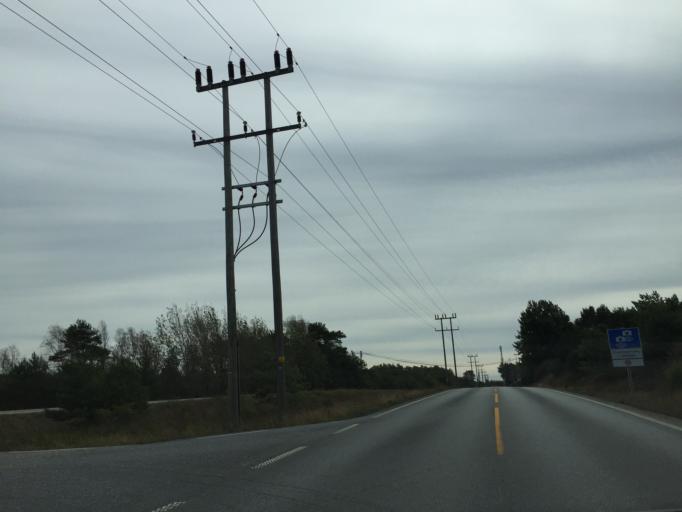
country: NO
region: Ostfold
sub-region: Hvaler
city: Skjaerhalden
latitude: 59.0519
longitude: 10.9498
